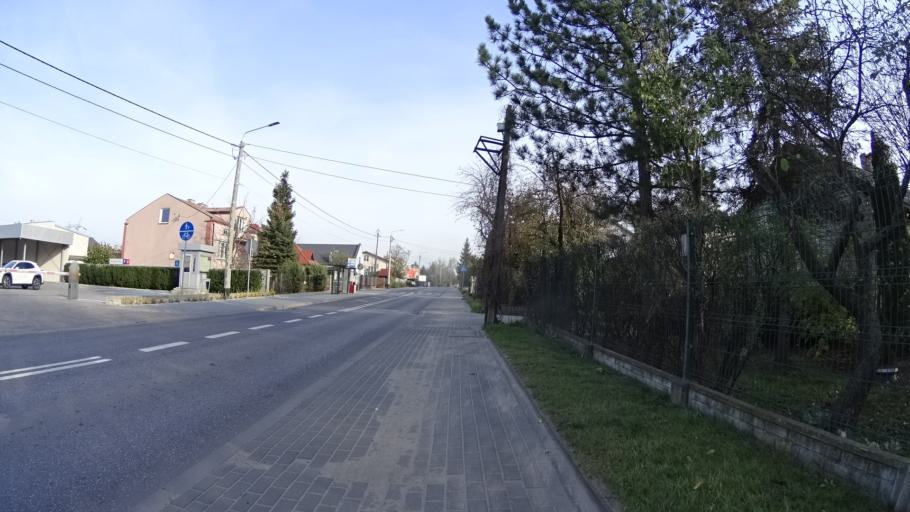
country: PL
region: Masovian Voivodeship
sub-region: Powiat warszawski zachodni
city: Babice
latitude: 52.2882
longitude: 20.8704
